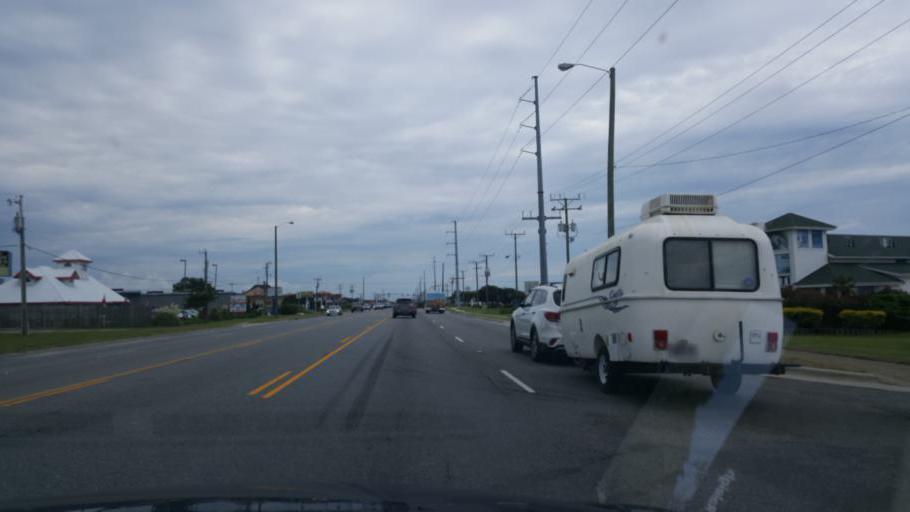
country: US
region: North Carolina
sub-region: Dare County
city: Kill Devil Hills
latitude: 36.0055
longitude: -75.6560
